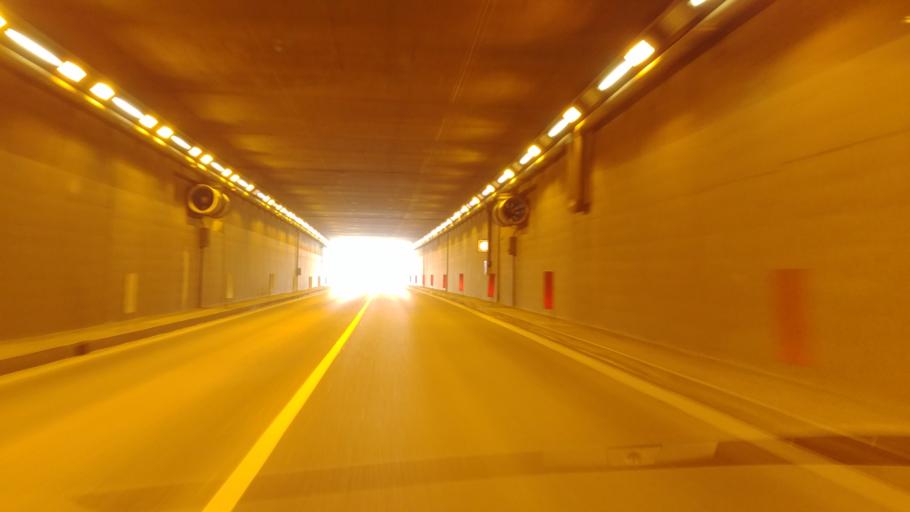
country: IT
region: Piedmont
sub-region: Provincia di Cuneo
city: Cuneo
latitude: 44.3756
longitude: 7.5380
